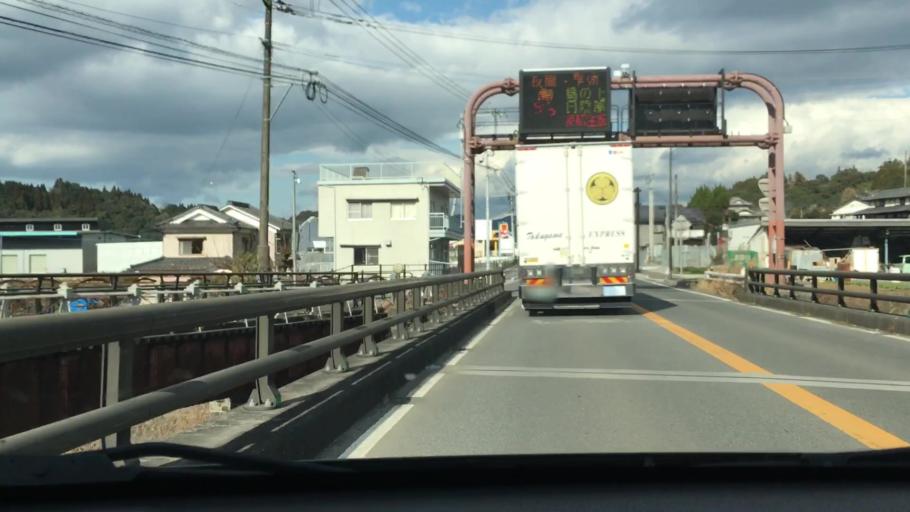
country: JP
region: Oita
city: Usuki
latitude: 33.0336
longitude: 131.6891
